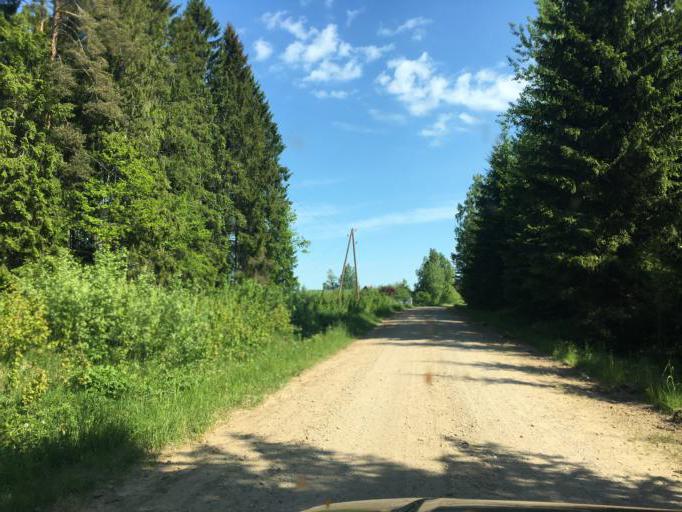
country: LV
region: Talsu Rajons
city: Talsi
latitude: 57.3199
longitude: 22.4454
